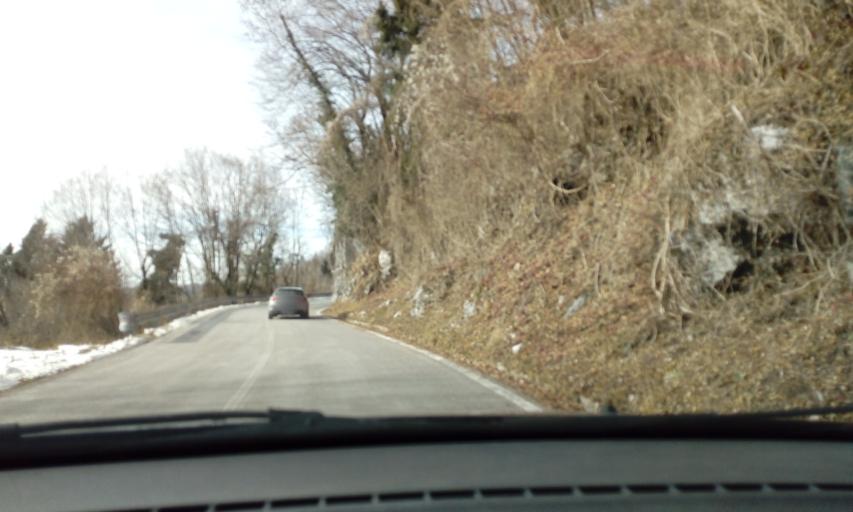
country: IT
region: Friuli Venezia Giulia
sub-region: Provincia di Udine
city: Savogna
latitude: 46.1927
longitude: 13.5430
